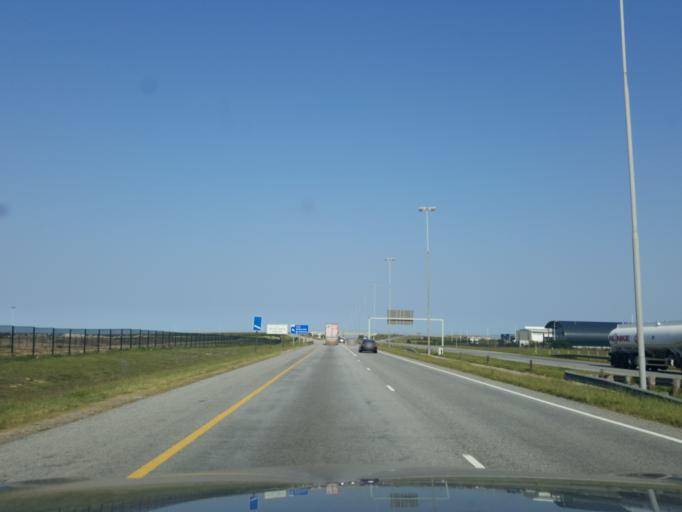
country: ZA
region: Eastern Cape
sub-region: Nelson Mandela Bay Metropolitan Municipality
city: Port Elizabeth
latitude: -33.8167
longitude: 25.6496
